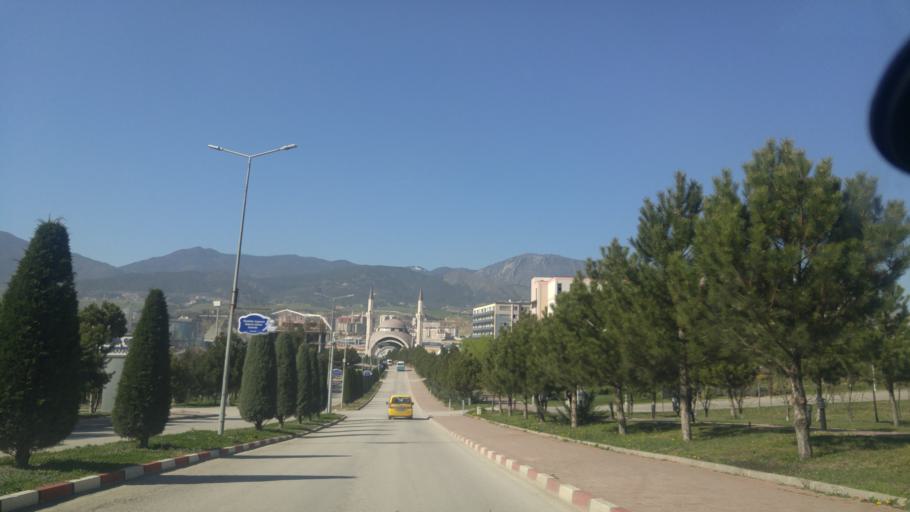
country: TR
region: Karabuk
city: Karabuk
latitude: 41.2086
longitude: 32.6568
